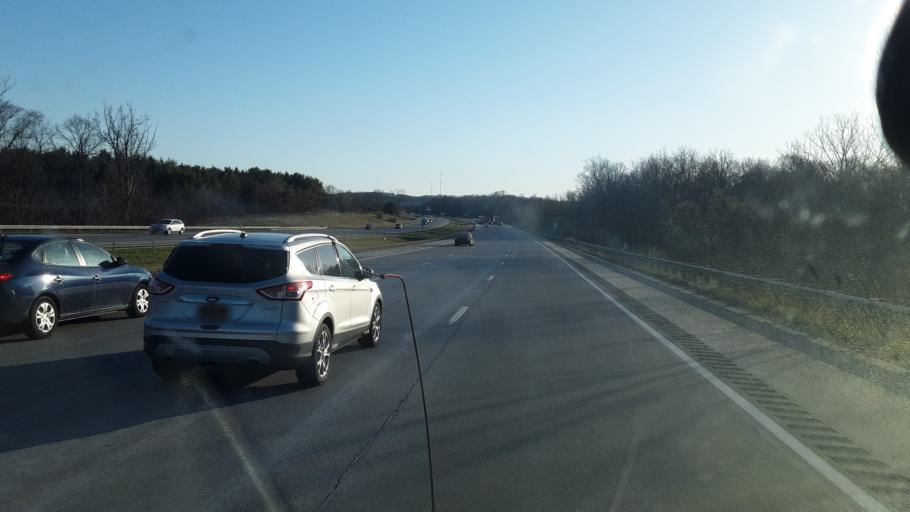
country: US
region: Ohio
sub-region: Wayne County
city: West Salem
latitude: 40.9330
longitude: -82.1158
